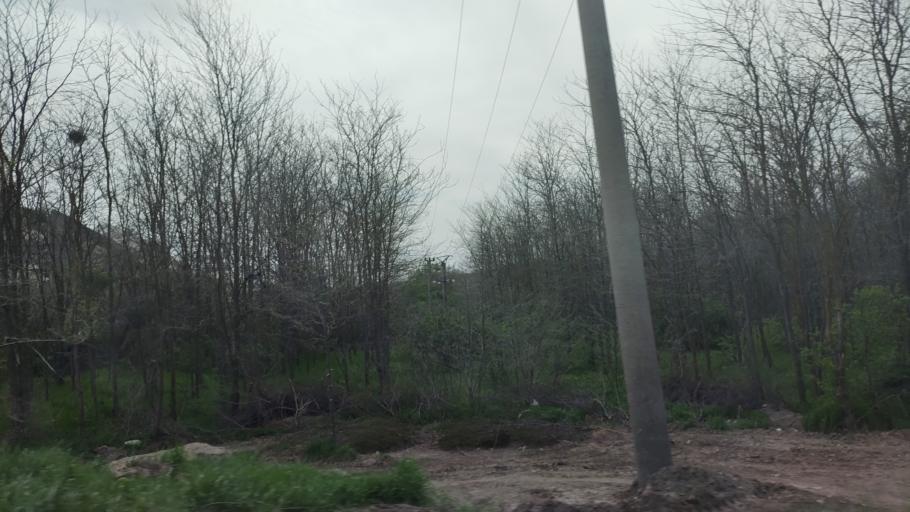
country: RO
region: Constanta
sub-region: Oras Murfatlar
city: Murfatlar
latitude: 44.1689
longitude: 28.4035
